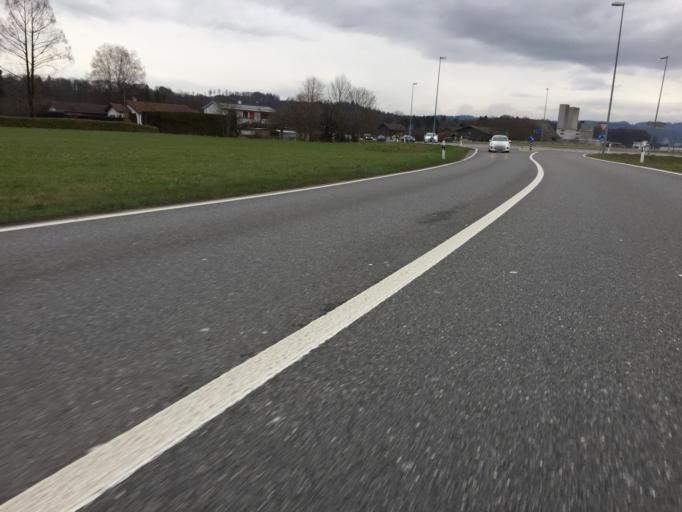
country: CH
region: Bern
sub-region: Emmental District
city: Kirchberg
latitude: 47.0758
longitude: 7.5818
